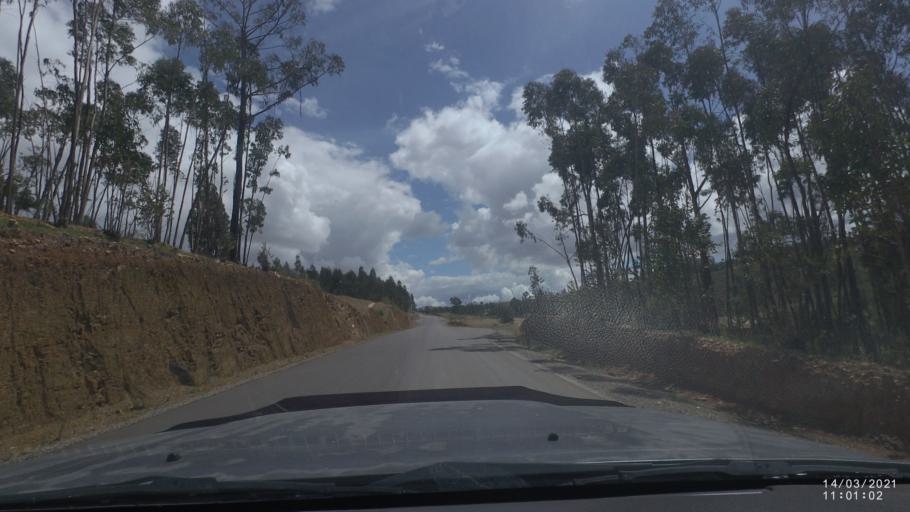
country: BO
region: Cochabamba
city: Tarata
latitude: -17.7993
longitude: -65.9632
